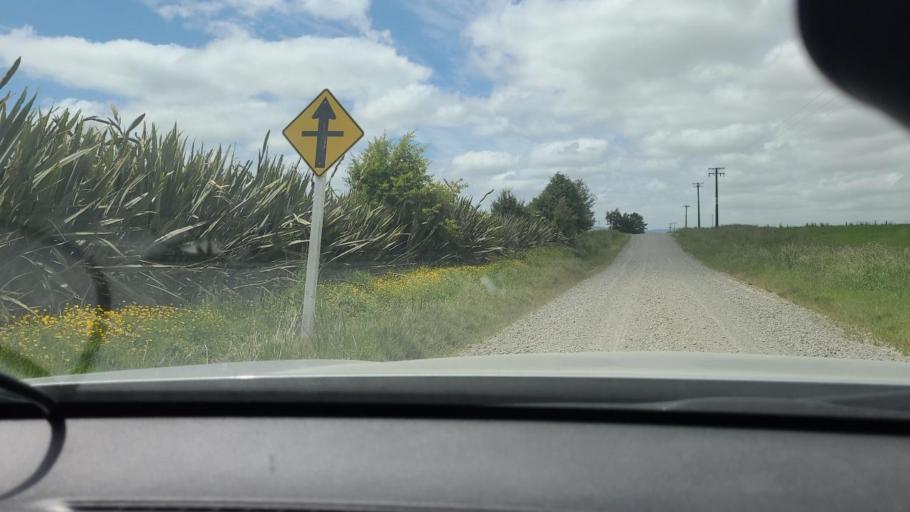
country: NZ
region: Southland
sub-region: Southland District
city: Winton
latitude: -45.9788
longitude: 168.0873
